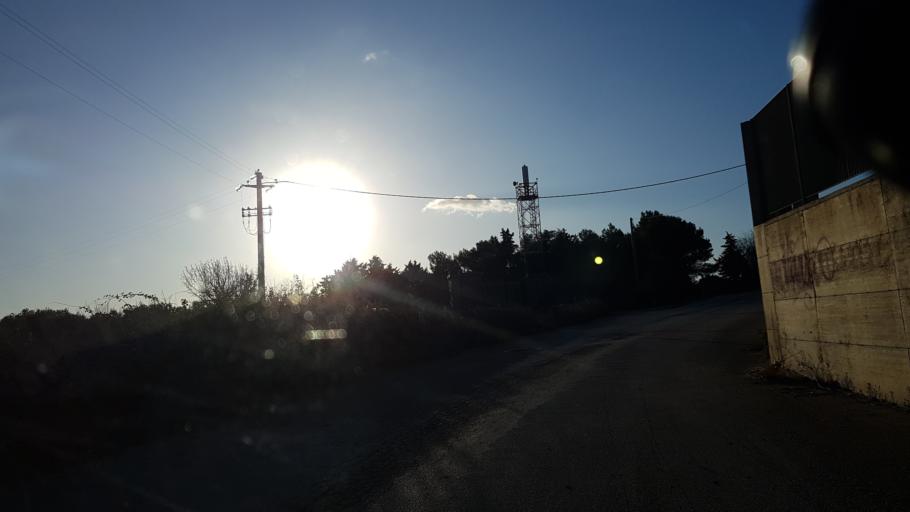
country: IT
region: Apulia
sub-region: Provincia di Bari
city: Gioia del Colle
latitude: 40.8015
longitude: 16.9028
